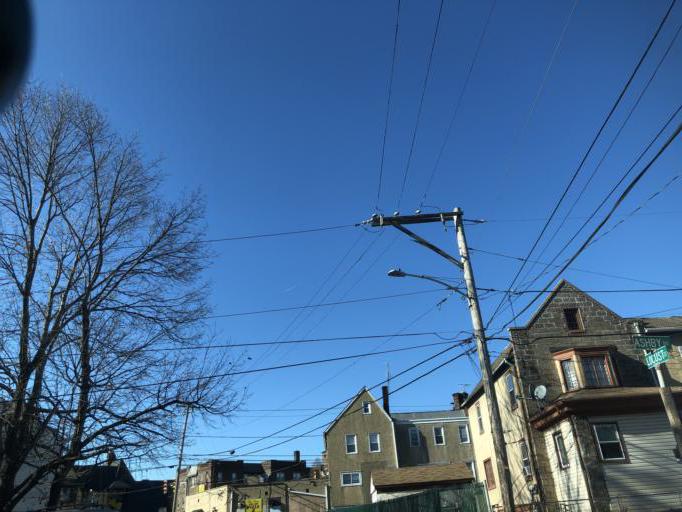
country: US
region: Pennsylvania
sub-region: Delaware County
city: East Lansdowne
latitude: 39.9548
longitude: -75.2635
